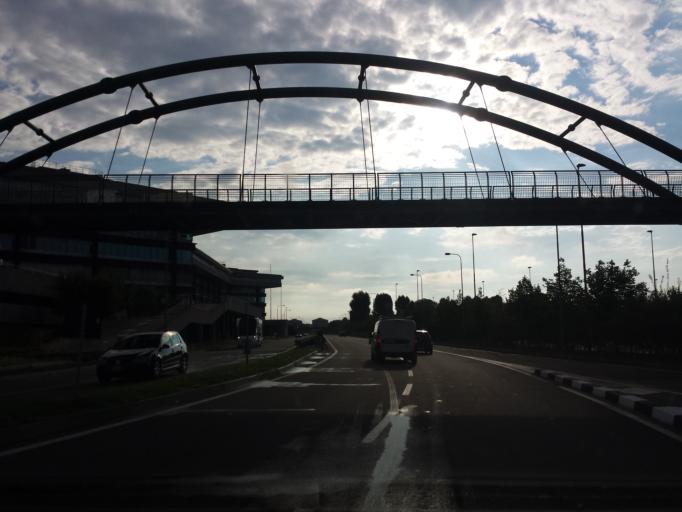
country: IT
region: Lombardy
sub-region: Citta metropolitana di Milano
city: Passirana
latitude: 45.5619
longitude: 9.0560
